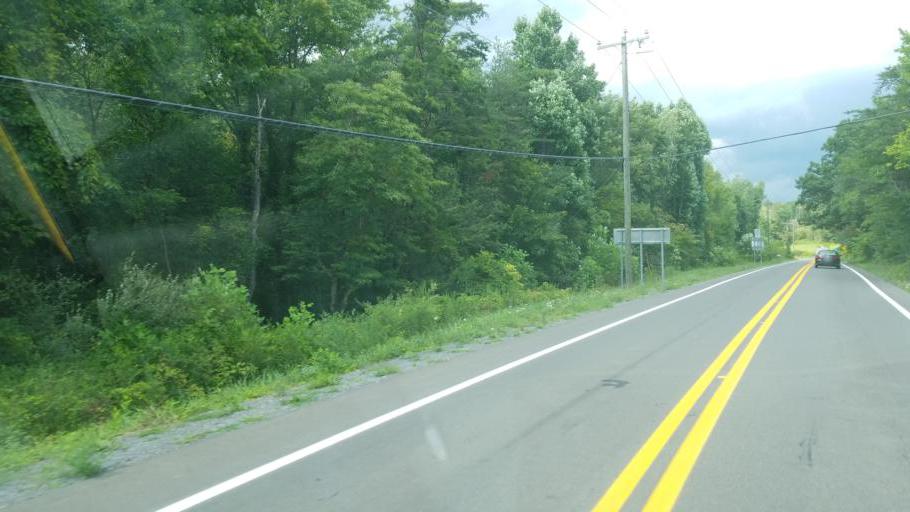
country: US
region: West Virginia
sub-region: Morgan County
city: Berkeley Springs
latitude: 39.4921
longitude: -78.4376
